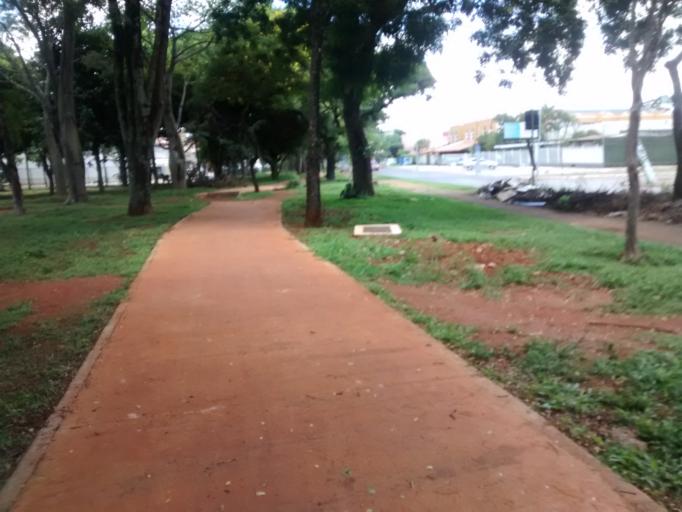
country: BR
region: Federal District
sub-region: Brasilia
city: Brasilia
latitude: -15.8058
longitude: -47.9022
